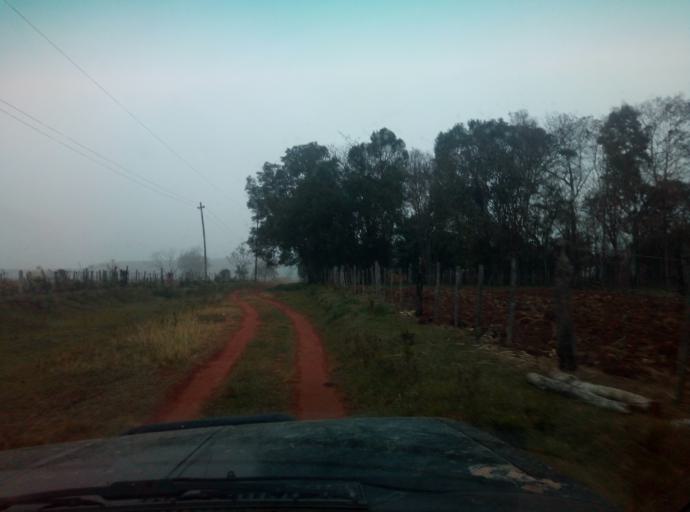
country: PY
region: Caaguazu
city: Doctor Cecilio Baez
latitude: -25.1581
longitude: -56.2615
